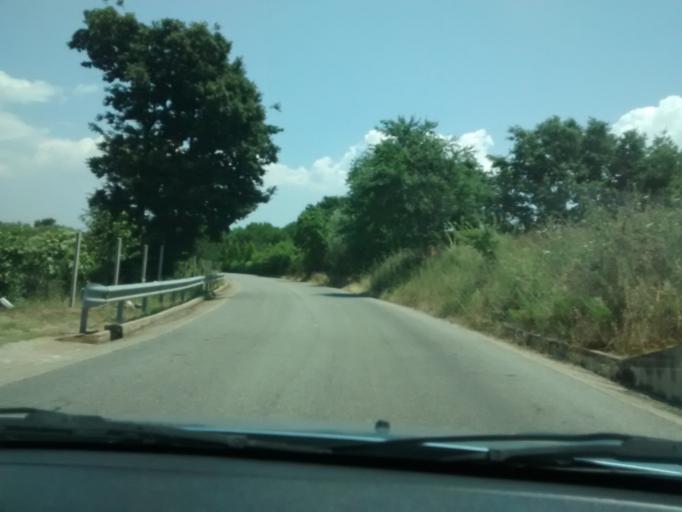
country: IT
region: Calabria
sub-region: Provincia di Catanzaro
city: Maida
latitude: 38.8951
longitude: 16.3973
